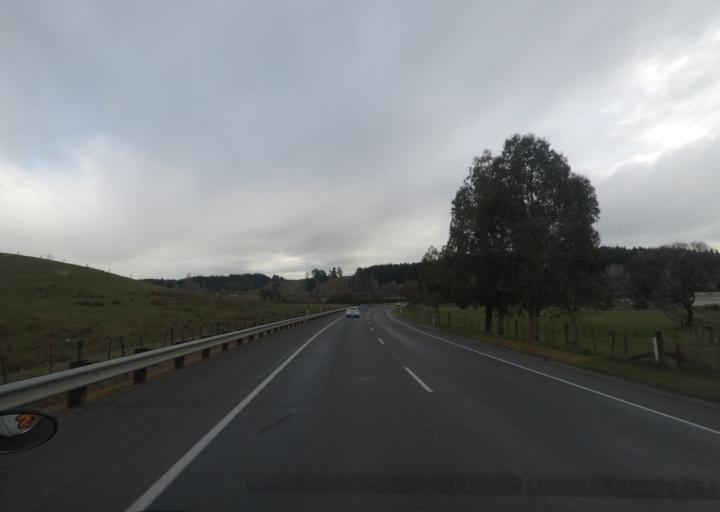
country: NZ
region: Tasman
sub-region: Tasman District
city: Mapua
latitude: -41.2816
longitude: 173.0721
